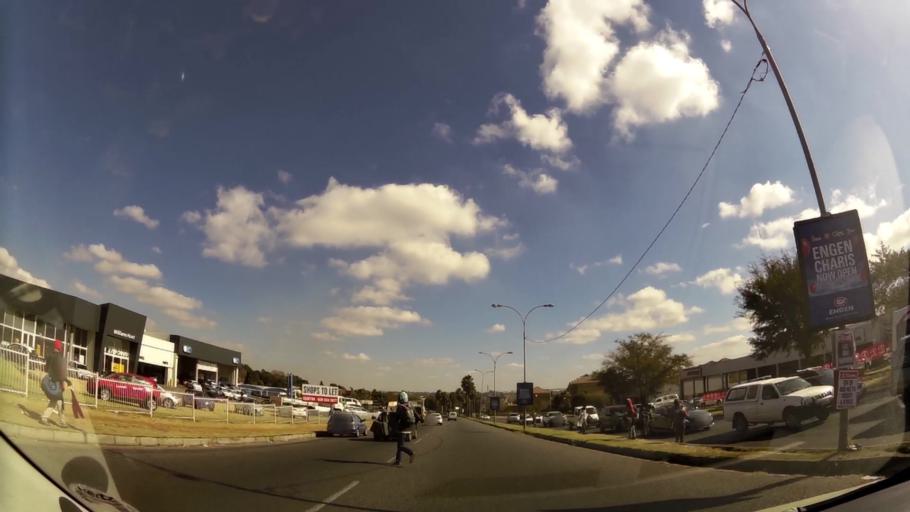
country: ZA
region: Gauteng
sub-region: City of Johannesburg Metropolitan Municipality
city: Roodepoort
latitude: -26.1270
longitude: 27.8453
